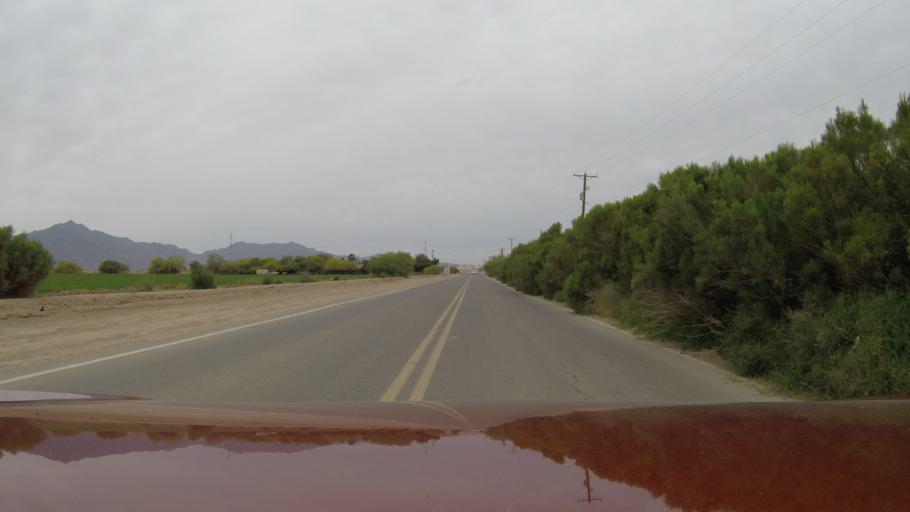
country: US
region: Arizona
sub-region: Maricopa County
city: Laveen
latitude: 33.3484
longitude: -112.1839
